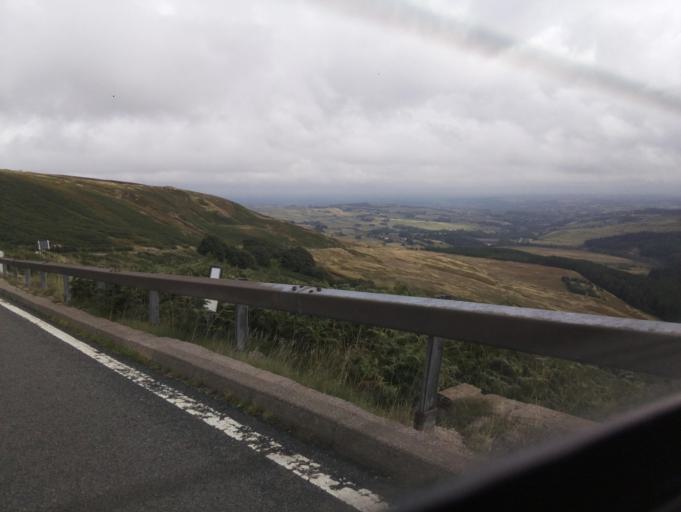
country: GB
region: England
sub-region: Kirklees
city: Meltham
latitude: 53.5332
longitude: -1.8545
